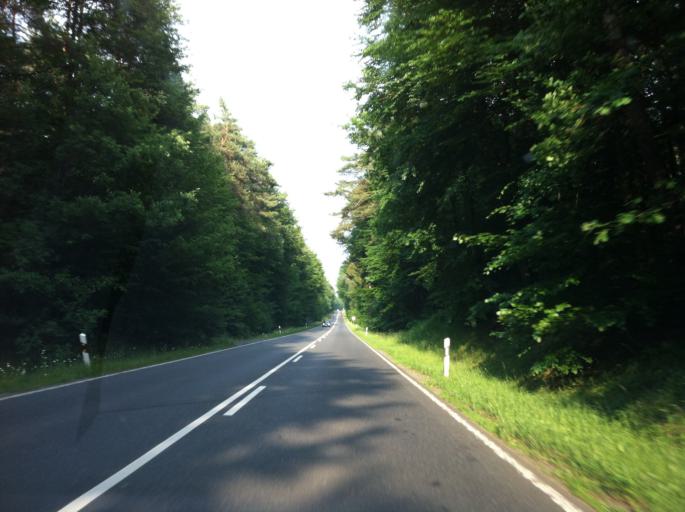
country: DE
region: Hesse
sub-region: Regierungsbezirk Darmstadt
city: Schaafheim
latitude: 49.9587
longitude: 9.0259
